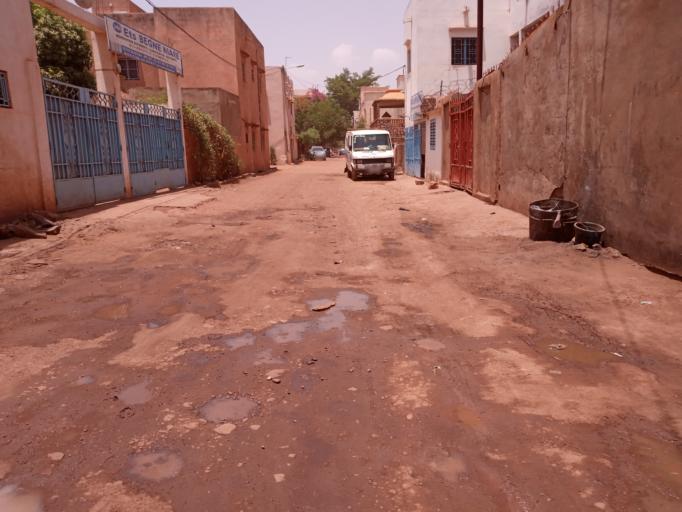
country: ML
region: Bamako
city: Bamako
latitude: 12.6512
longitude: -7.9517
